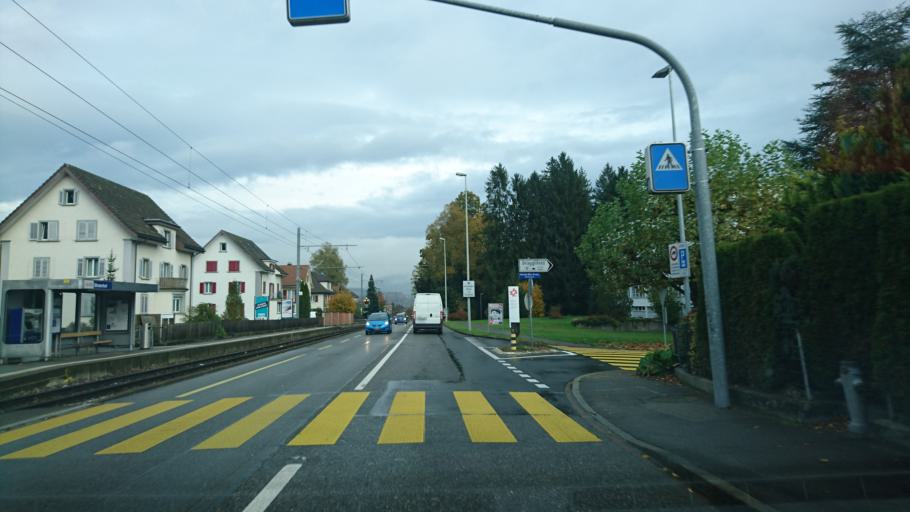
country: CH
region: Aargau
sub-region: Bezirk Aarau
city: Aarau
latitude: 47.3830
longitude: 8.0507
